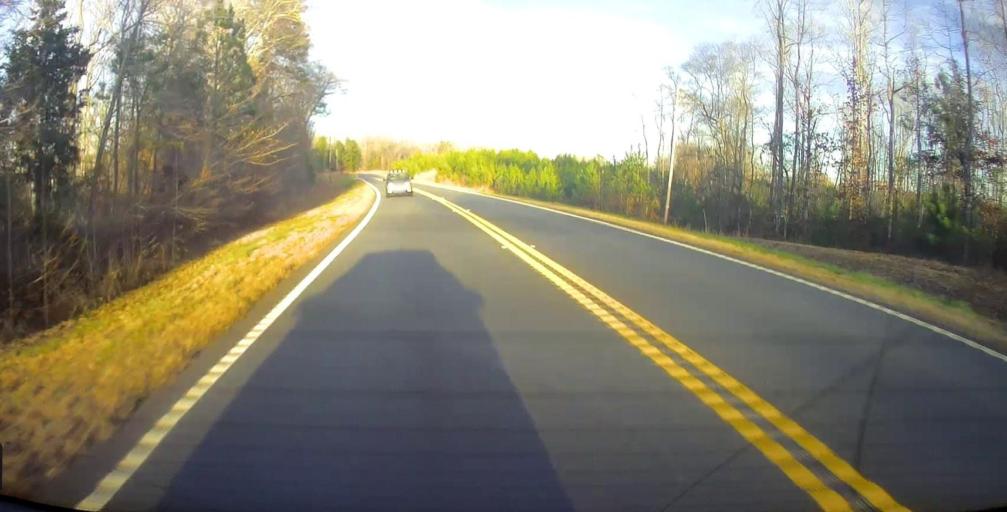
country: US
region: Georgia
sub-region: Talbot County
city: Sardis
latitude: 32.7204
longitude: -84.6607
